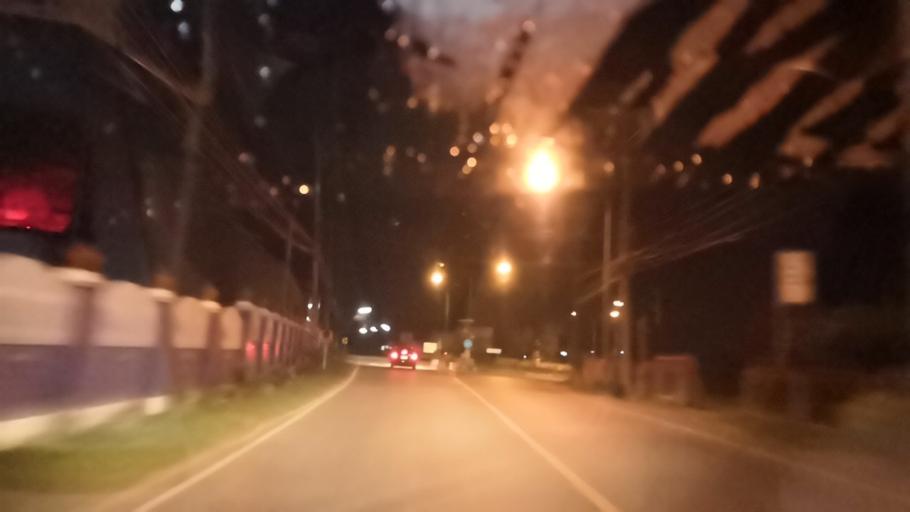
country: TH
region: Mae Hong Son
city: Khun Yuam
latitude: 18.8322
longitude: 97.9362
